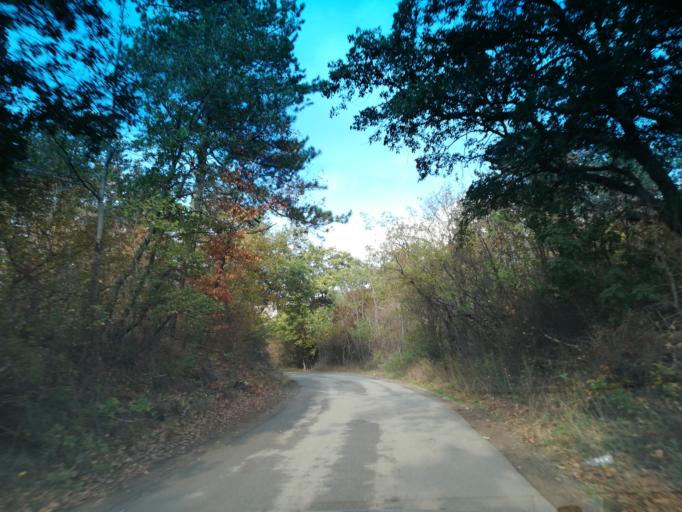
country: BG
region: Stara Zagora
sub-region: Obshtina Nikolaevo
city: Elkhovo
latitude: 42.3215
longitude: 25.4014
